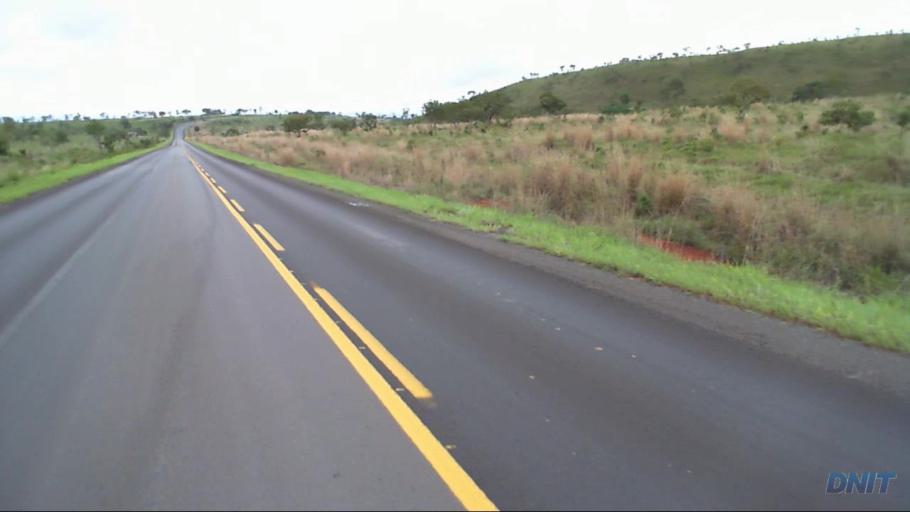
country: BR
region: Goias
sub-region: Padre Bernardo
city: Padre Bernardo
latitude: -15.2073
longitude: -48.4668
